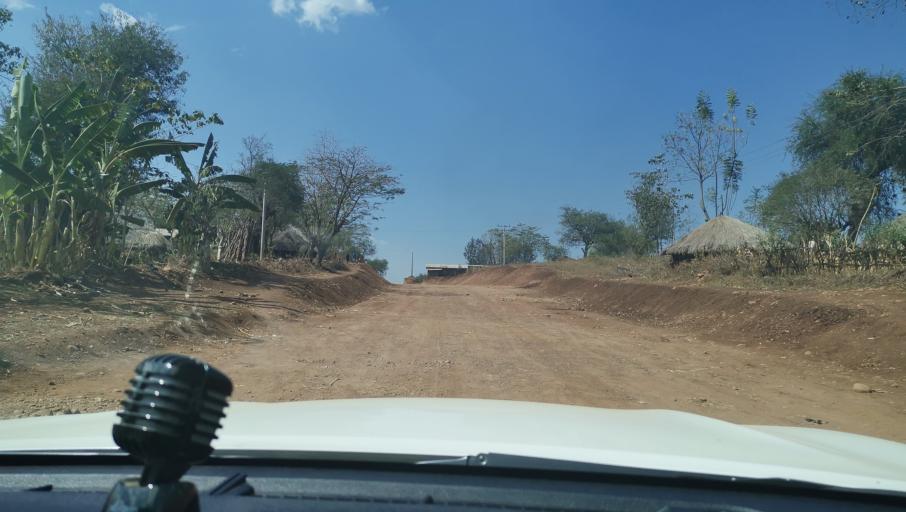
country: ET
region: Southern Nations, Nationalities, and People's Region
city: Arba Minch'
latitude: 6.3380
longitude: 37.2923
